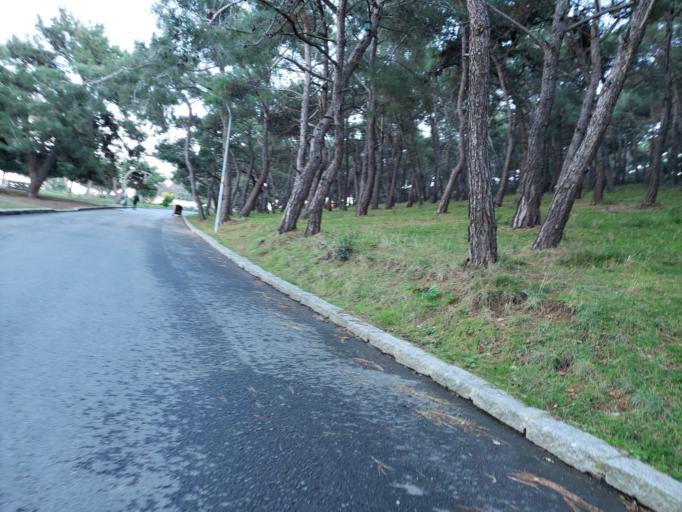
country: TR
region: Istanbul
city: Adalan
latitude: 40.8843
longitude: 29.0964
